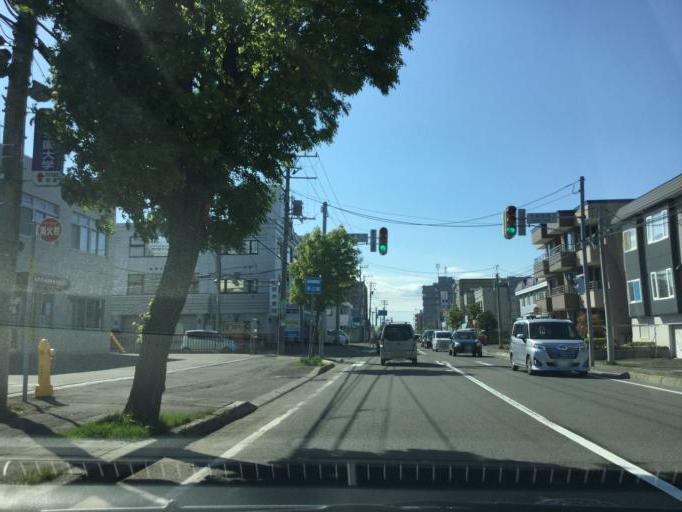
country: JP
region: Hokkaido
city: Sapporo
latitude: 43.0201
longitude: 141.4489
